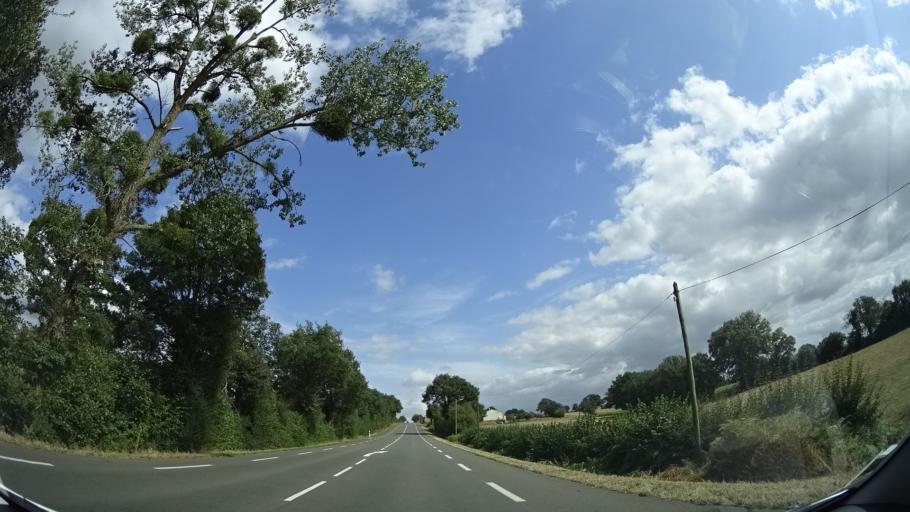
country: FR
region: Pays de la Loire
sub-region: Departement de la Mayenne
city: Sainte-Suzanne
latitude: 48.0339
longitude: -0.3736
